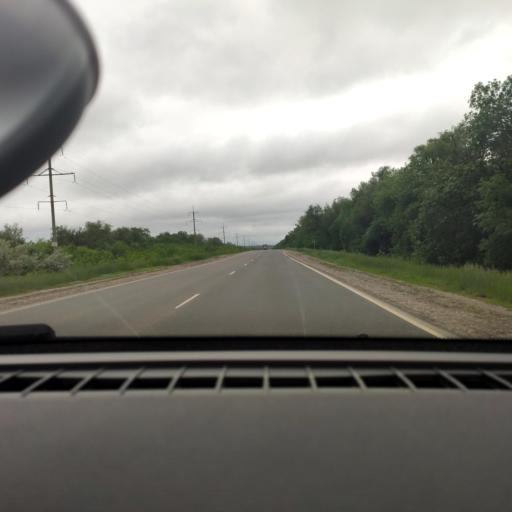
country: RU
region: Samara
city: Dubovyy Umet
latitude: 53.1018
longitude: 50.2551
